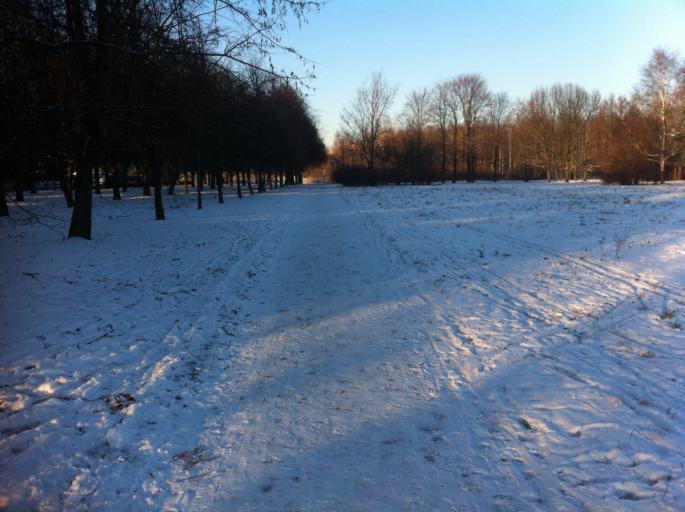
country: RU
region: St.-Petersburg
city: Uritsk
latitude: 59.8516
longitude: 30.1703
